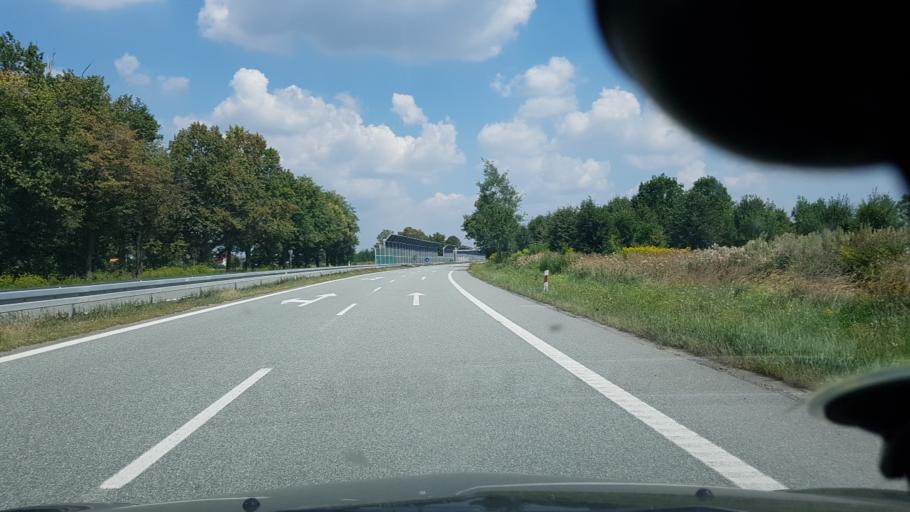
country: PL
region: Silesian Voivodeship
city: Gardawice
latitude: 50.1038
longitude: 18.7824
